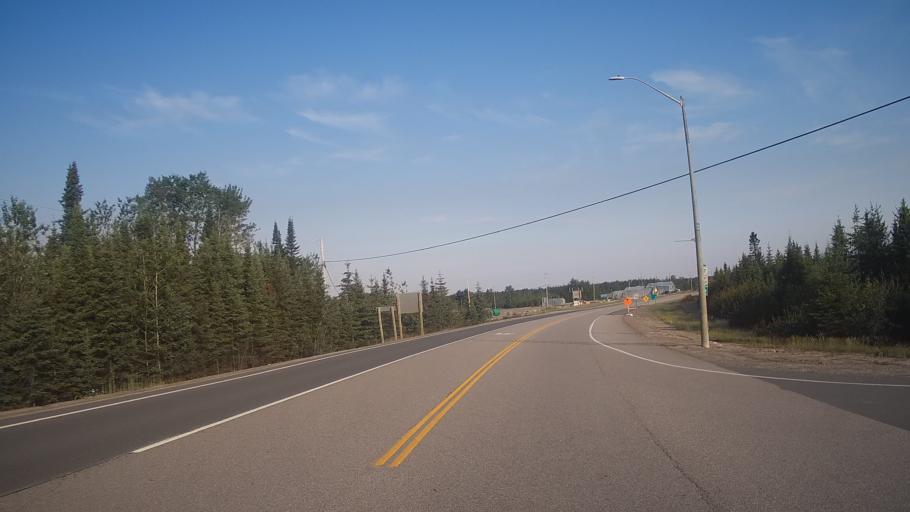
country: CA
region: Ontario
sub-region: Rainy River District
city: Atikokan
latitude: 49.4055
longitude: -91.6347
